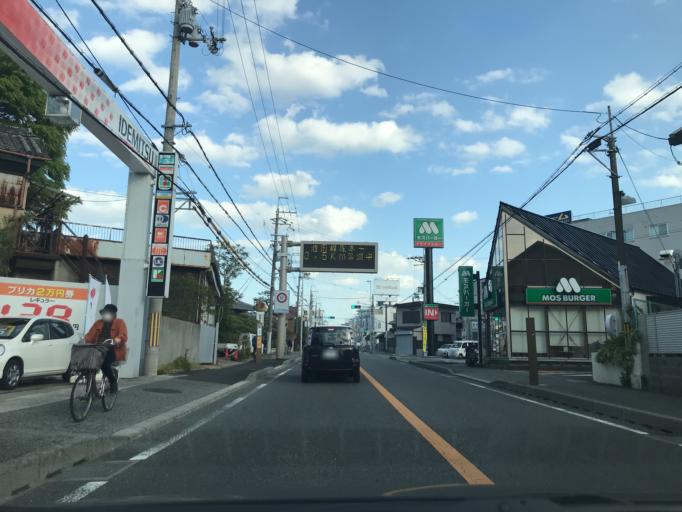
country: JP
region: Osaka
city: Ikeda
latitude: 34.8160
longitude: 135.4367
